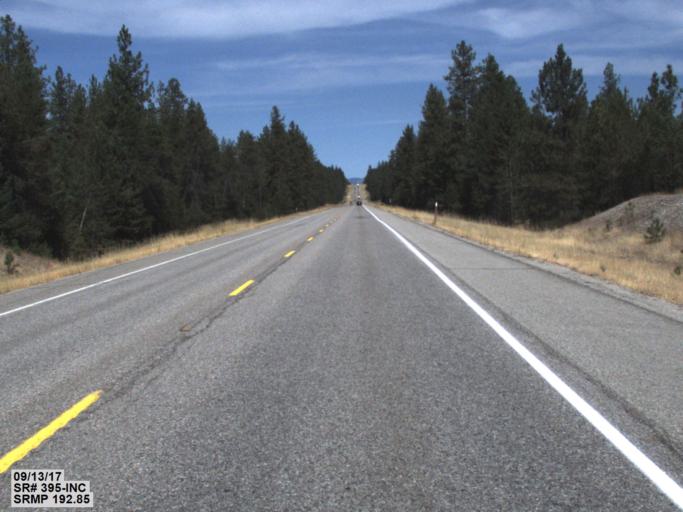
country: US
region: Washington
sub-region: Stevens County
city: Chewelah
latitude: 48.0914
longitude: -117.6353
